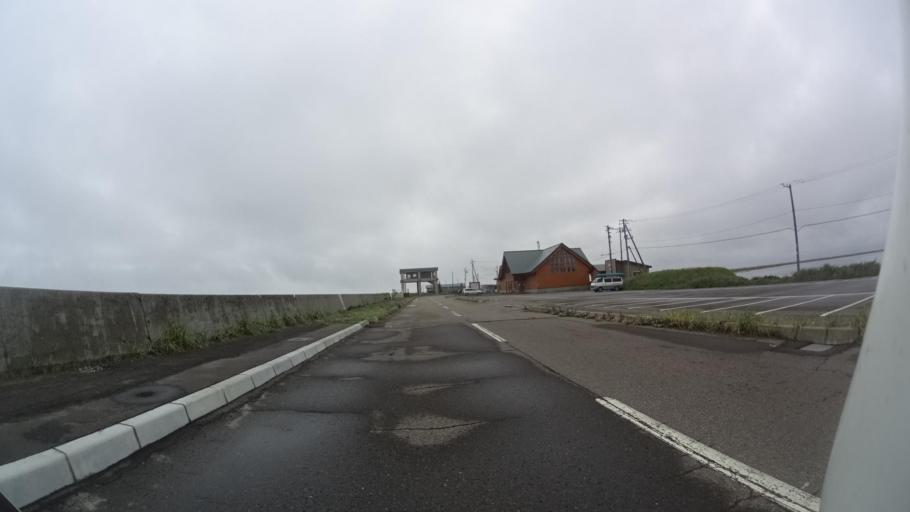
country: JP
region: Hokkaido
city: Shibetsu
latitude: 43.5912
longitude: 145.3343
